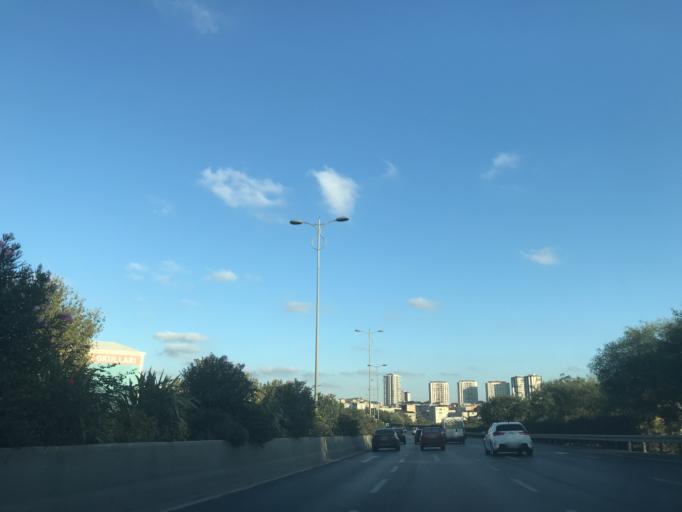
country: TR
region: Istanbul
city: Mahmutbey
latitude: 41.0577
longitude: 28.8464
